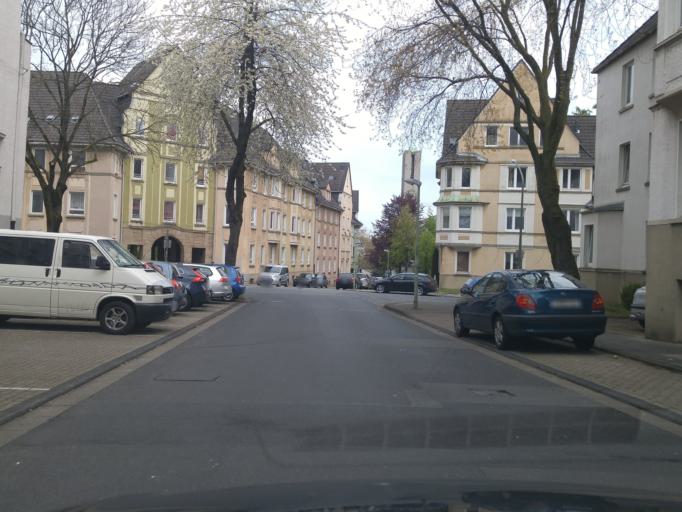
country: DE
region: North Rhine-Westphalia
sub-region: Regierungsbezirk Dusseldorf
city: Essen
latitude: 51.4413
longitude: 6.9901
